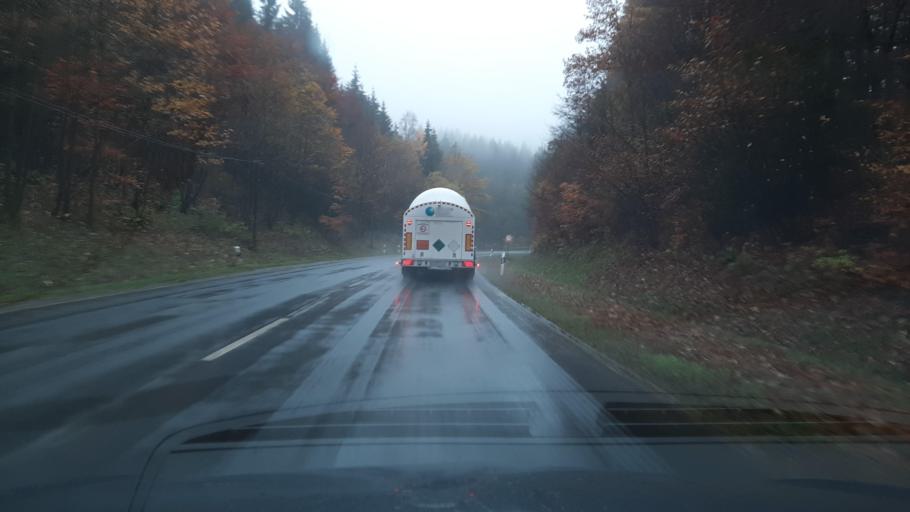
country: DE
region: North Rhine-Westphalia
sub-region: Regierungsbezirk Arnsberg
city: Bad Fredeburg
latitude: 51.2121
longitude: 8.3388
